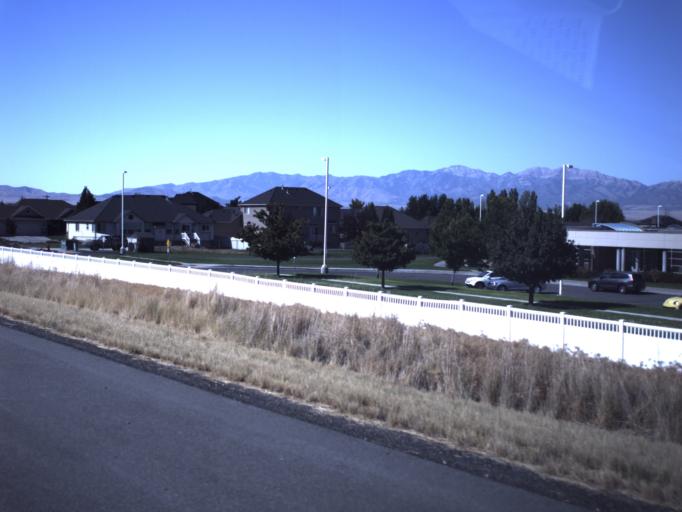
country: US
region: Utah
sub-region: Tooele County
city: Stansbury park
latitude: 40.6264
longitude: -112.2924
